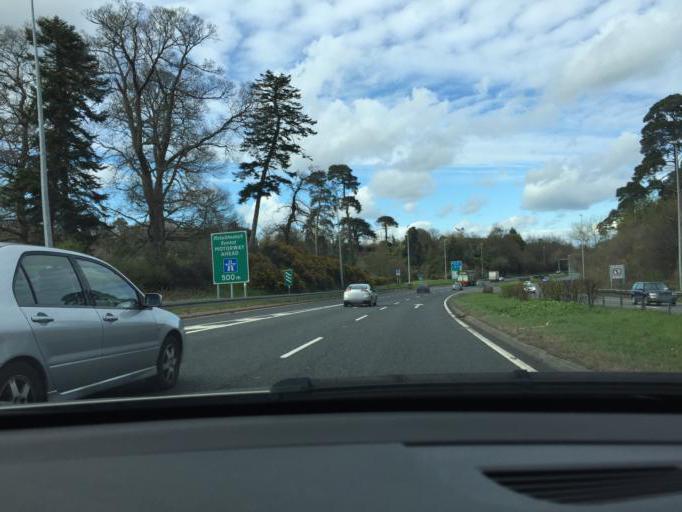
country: IE
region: Leinster
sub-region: Wicklow
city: Kilmacanoge
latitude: 53.1896
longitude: -6.1387
